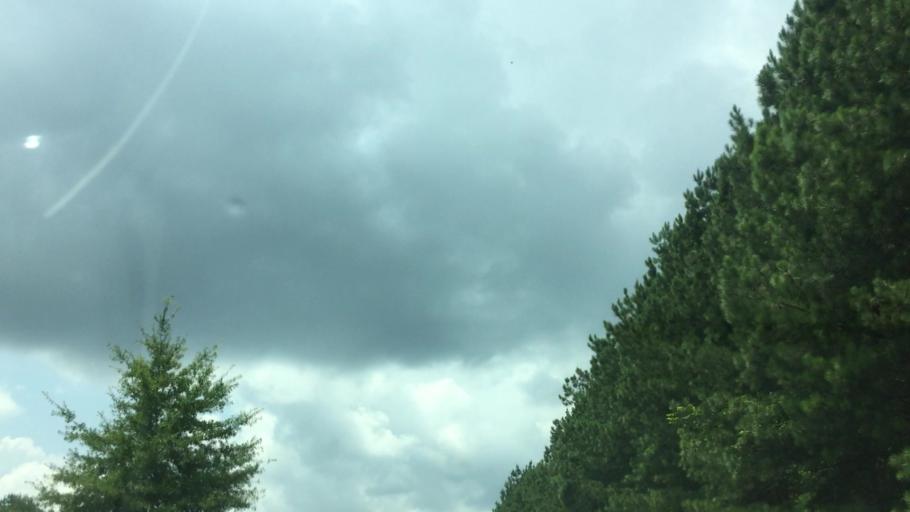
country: US
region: Georgia
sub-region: Fulton County
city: Fairburn
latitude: 33.6047
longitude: -84.6256
